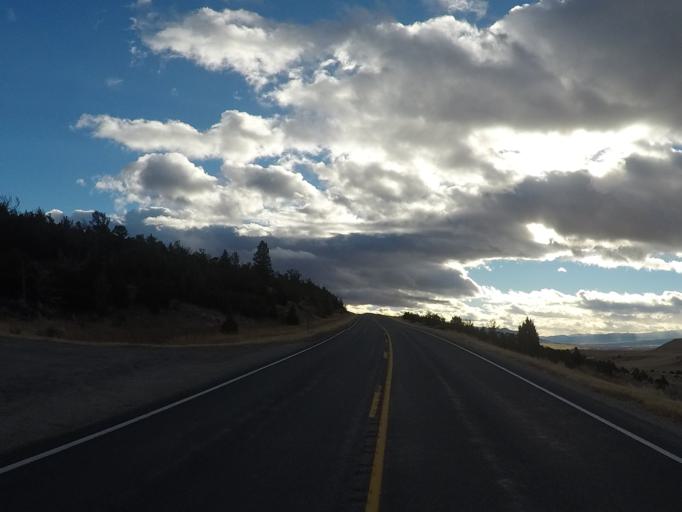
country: US
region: Montana
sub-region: Jefferson County
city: Whitehall
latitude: 45.8941
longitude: -111.9625
